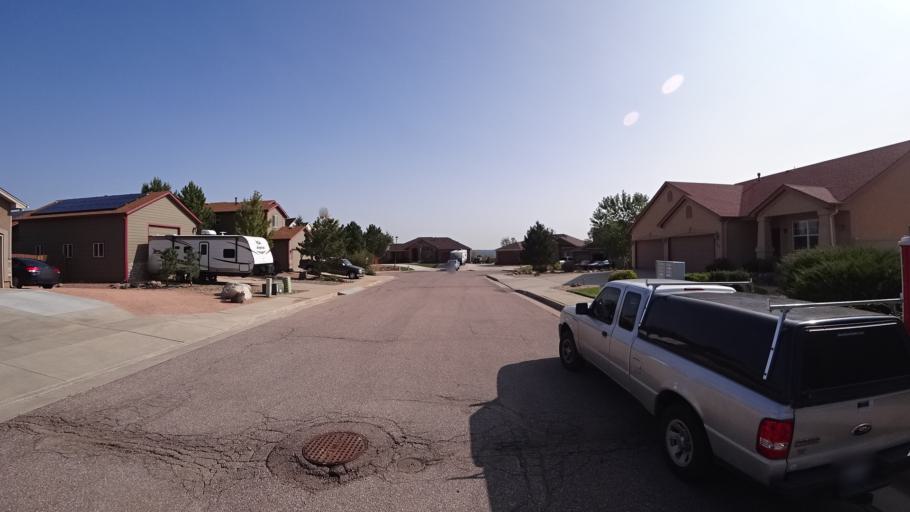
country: US
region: Colorado
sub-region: El Paso County
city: Colorado Springs
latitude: 38.8279
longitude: -104.8521
